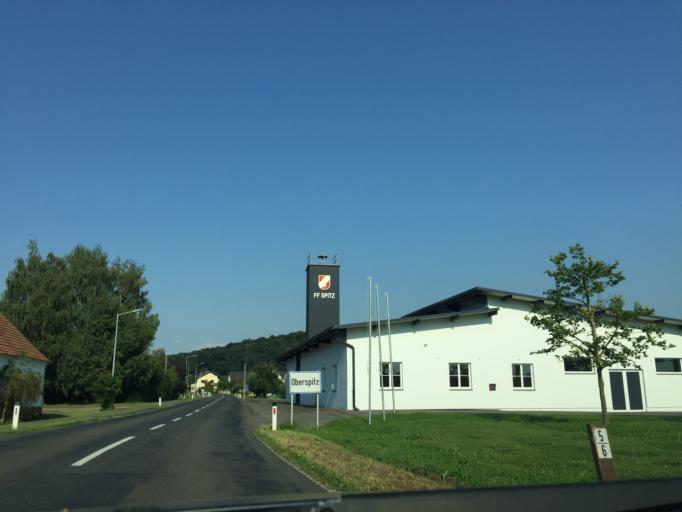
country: AT
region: Styria
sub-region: Politischer Bezirk Suedoststeiermark
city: Deutsch Goritz
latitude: 46.7616
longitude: 15.8451
